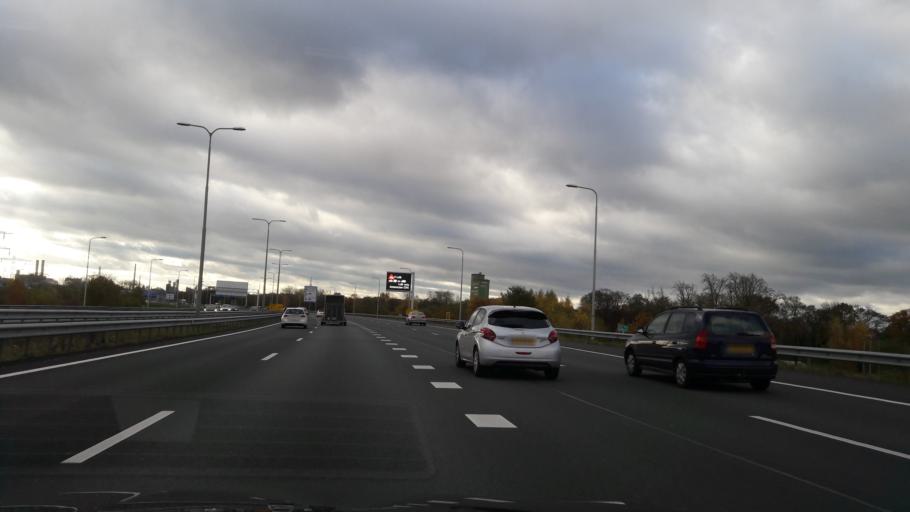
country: NL
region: Limburg
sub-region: Gemeente Stein
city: Urmond
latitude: 50.9841
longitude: 5.7826
